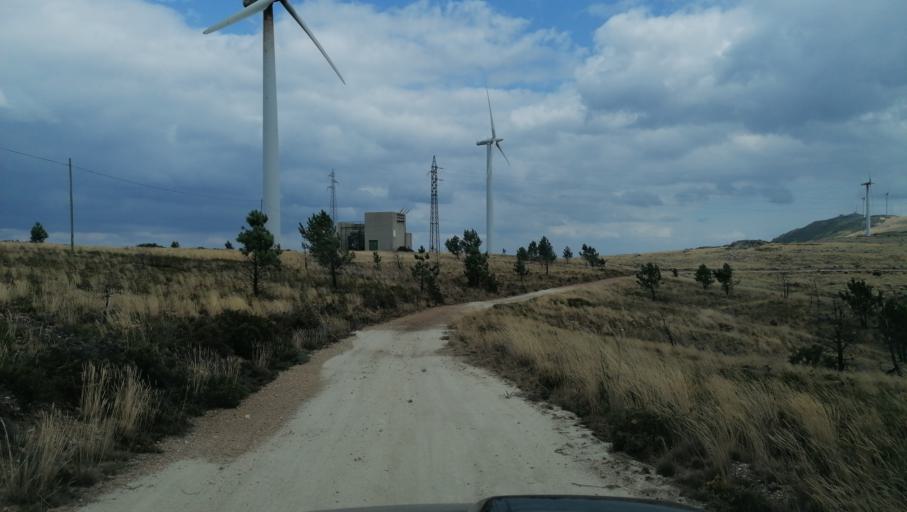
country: PT
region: Vila Real
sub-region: Vila Pouca de Aguiar
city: Vila Pouca de Aguiar
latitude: 41.5363
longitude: -7.7138
